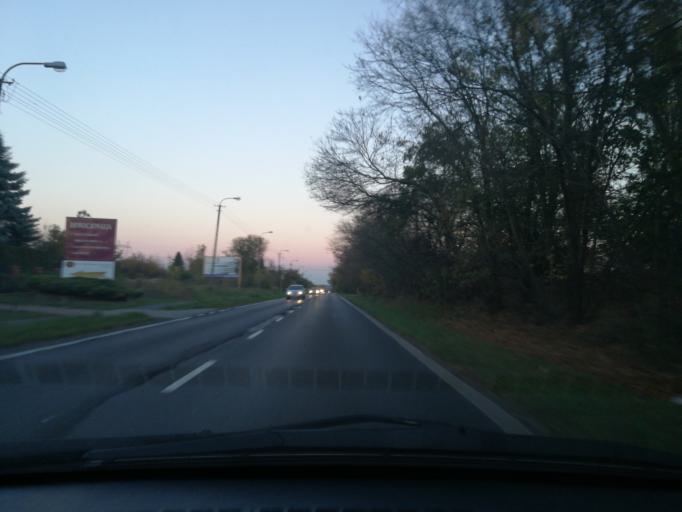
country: PL
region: Lodz Voivodeship
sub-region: Powiat lodzki wschodni
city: Andrespol
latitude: 51.7946
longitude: 19.5774
